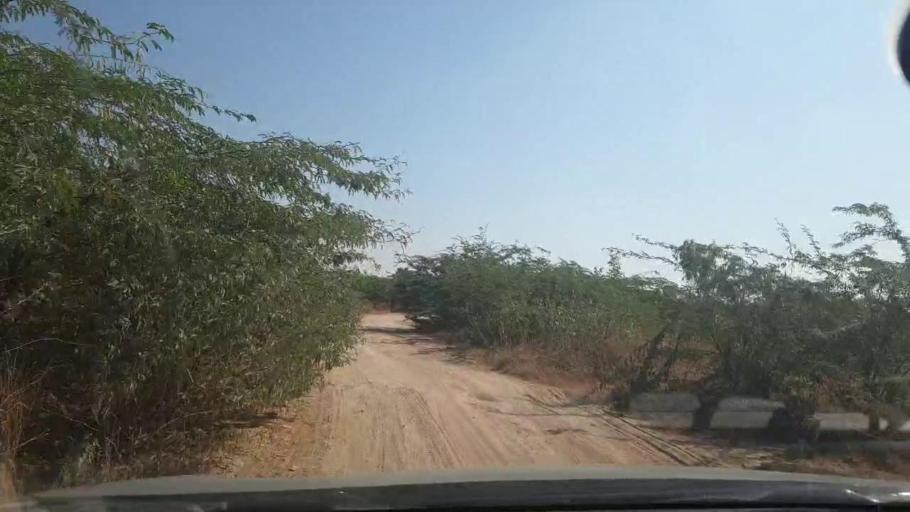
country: PK
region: Sindh
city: Malir Cantonment
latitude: 25.1678
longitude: 67.2040
